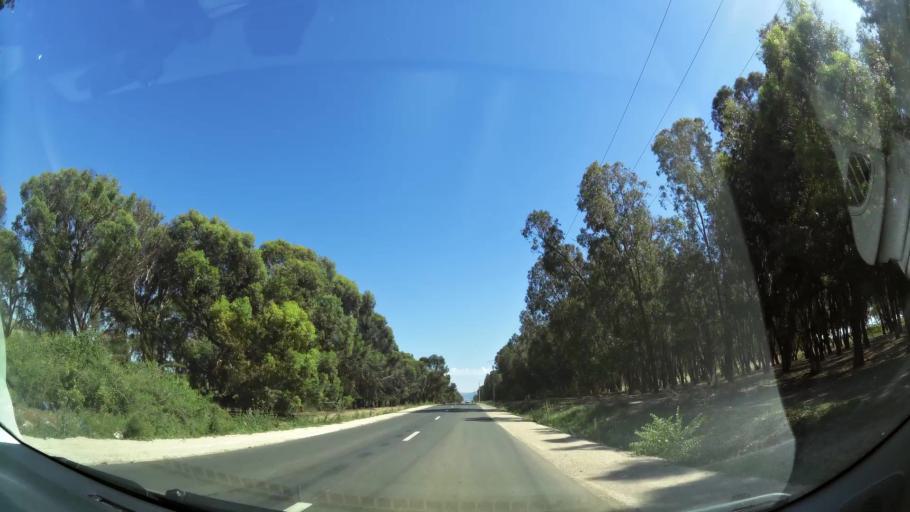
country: MA
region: Oriental
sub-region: Berkane-Taourirt
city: Madagh
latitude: 35.0044
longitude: -2.3974
